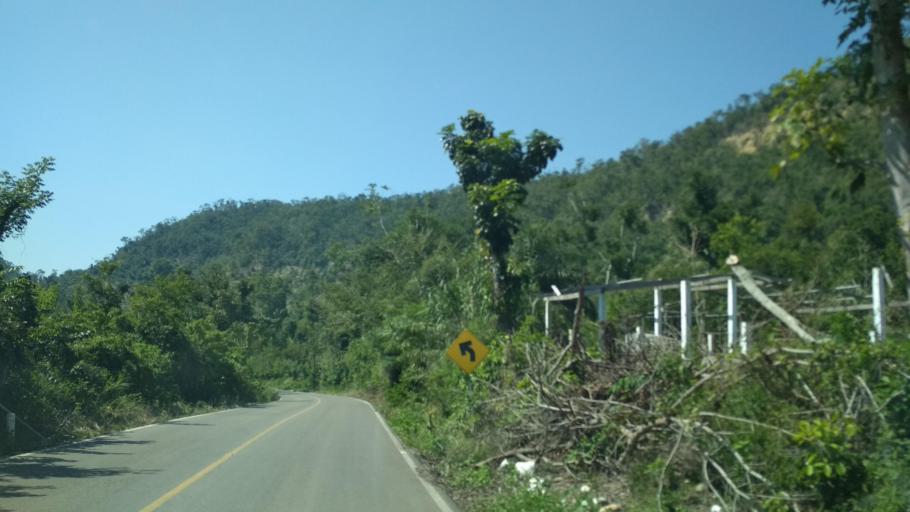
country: MX
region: Veracruz
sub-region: Papantla
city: Polutla
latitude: 20.4706
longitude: -97.2225
